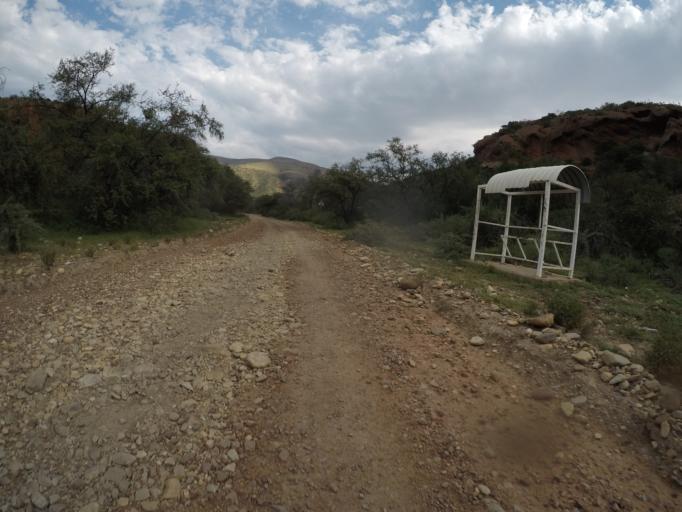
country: ZA
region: Eastern Cape
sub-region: Cacadu District Municipality
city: Kareedouw
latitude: -33.6006
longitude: 24.2078
